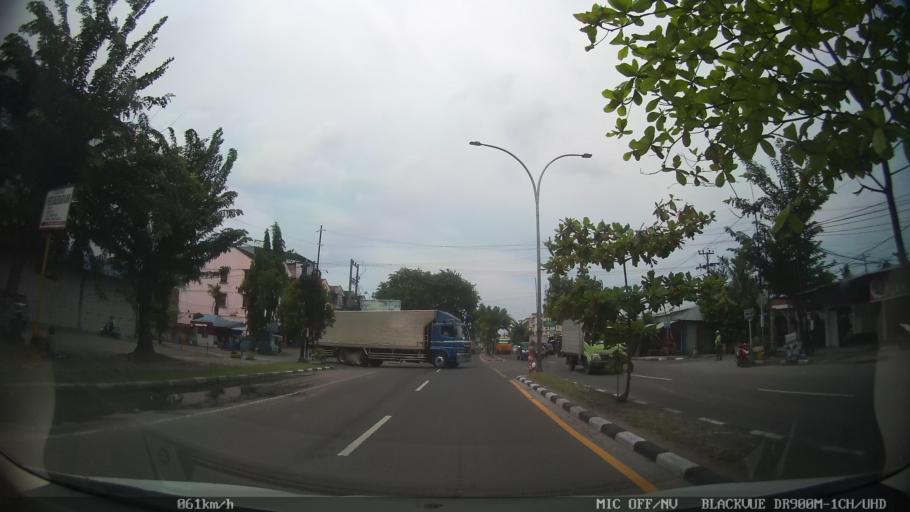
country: ID
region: North Sumatra
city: Medan
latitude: 3.6356
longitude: 98.6812
